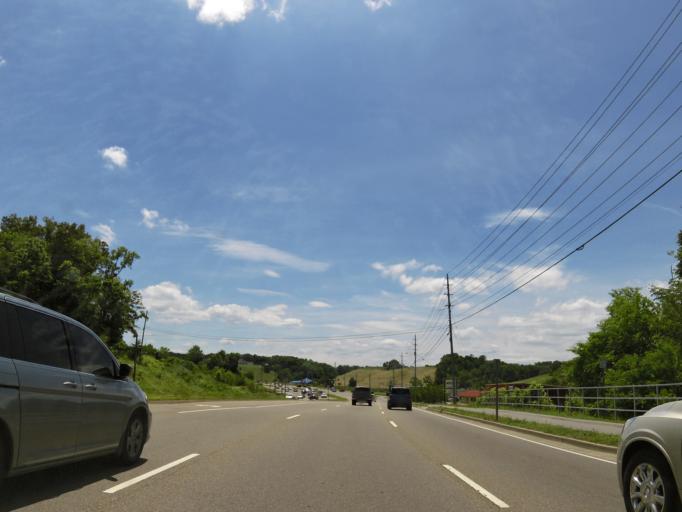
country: US
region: Tennessee
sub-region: Sevier County
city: Sevierville
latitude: 35.8411
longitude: -83.5441
